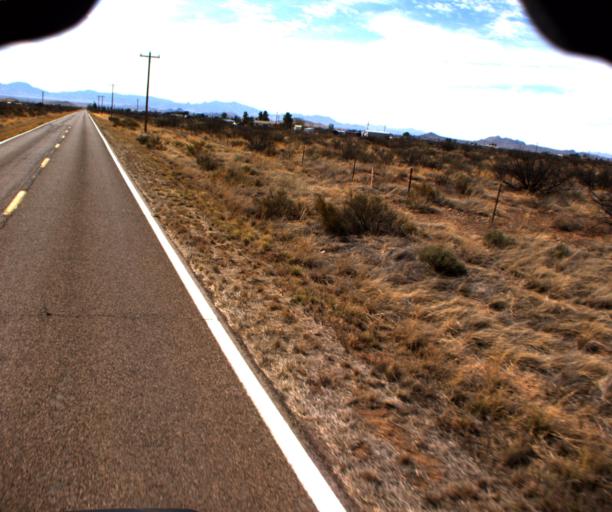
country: US
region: Arizona
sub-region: Cochise County
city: Willcox
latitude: 31.8762
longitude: -109.6063
